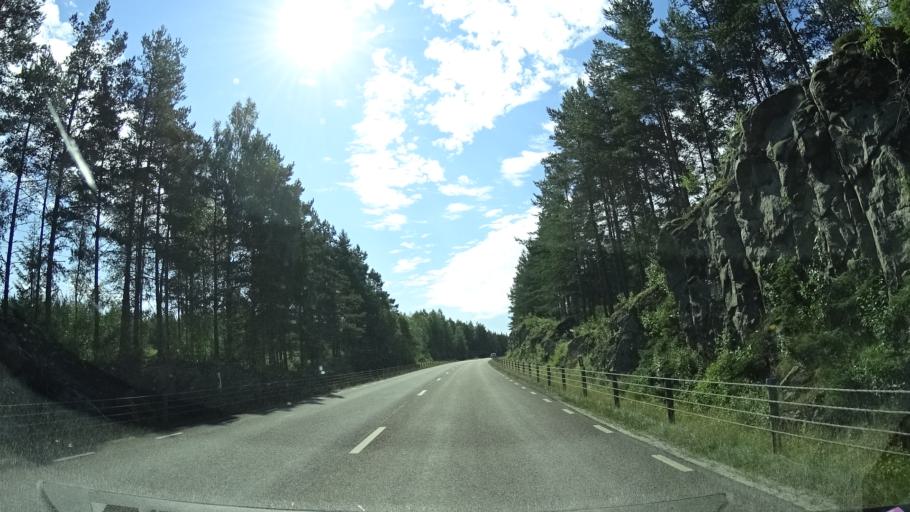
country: SE
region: Vaermland
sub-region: Arjangs Kommun
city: Arjaeng
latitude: 59.4457
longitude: 12.0745
